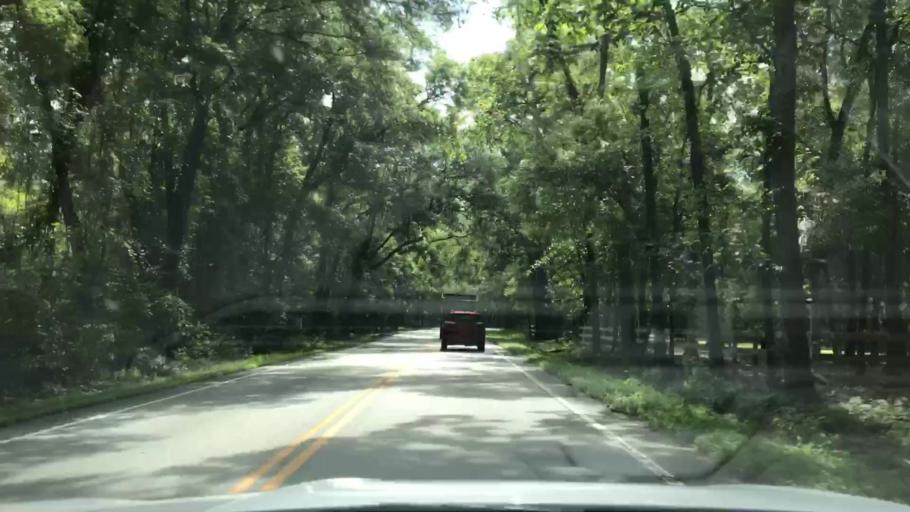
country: US
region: South Carolina
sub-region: Berkeley County
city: Ladson
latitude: 32.8883
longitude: -80.1189
